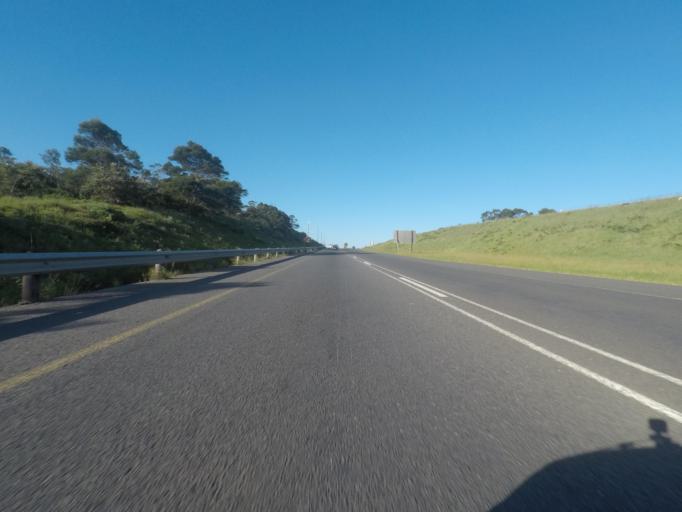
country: ZA
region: Eastern Cape
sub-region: Buffalo City Metropolitan Municipality
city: East London
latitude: -33.0423
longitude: 27.8295
